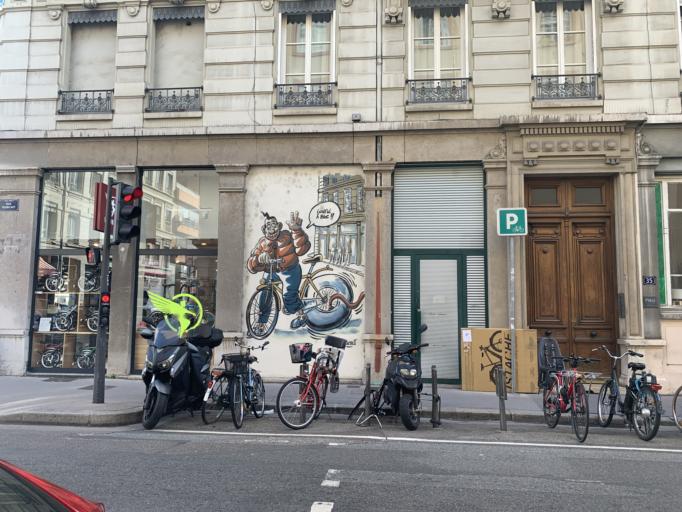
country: FR
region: Rhone-Alpes
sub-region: Departement du Rhone
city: Caluire-et-Cuire
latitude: 45.7699
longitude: 4.8473
